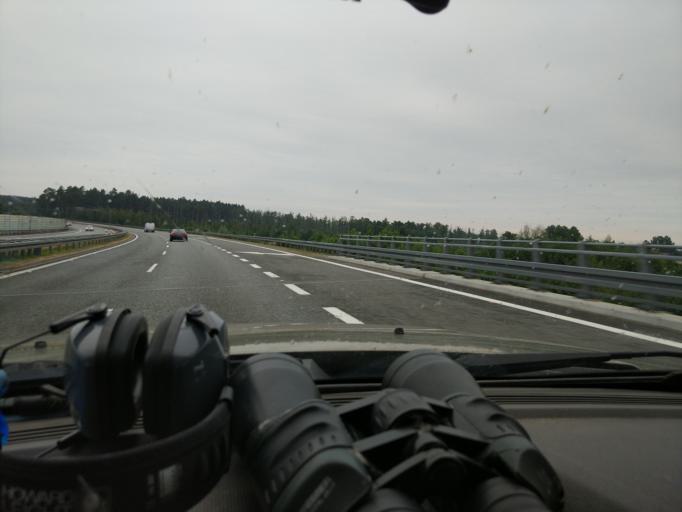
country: PL
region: Masovian Voivodeship
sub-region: Powiat wyszkowski
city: Wyszkow
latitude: 52.5591
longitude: 21.4657
